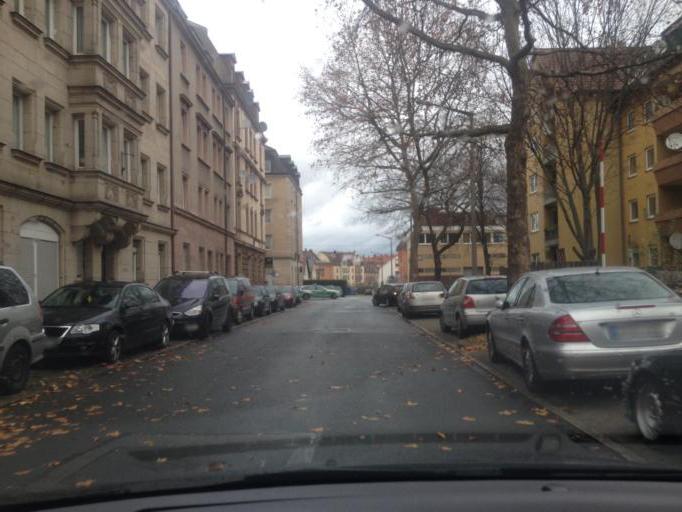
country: DE
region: Bavaria
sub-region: Regierungsbezirk Mittelfranken
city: Grossreuth bei Schweinau
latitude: 49.4343
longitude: 11.0508
